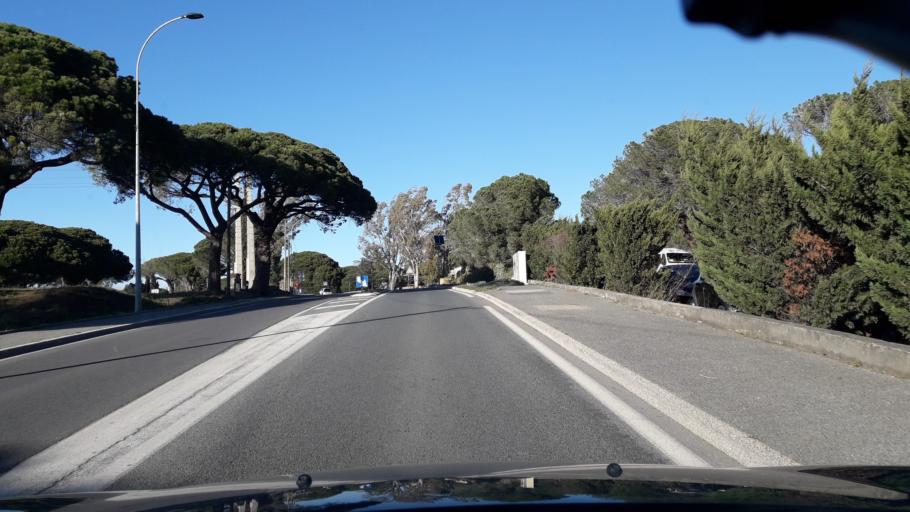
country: FR
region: Provence-Alpes-Cote d'Azur
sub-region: Departement du Var
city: Frejus
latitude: 43.4559
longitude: 6.7278
